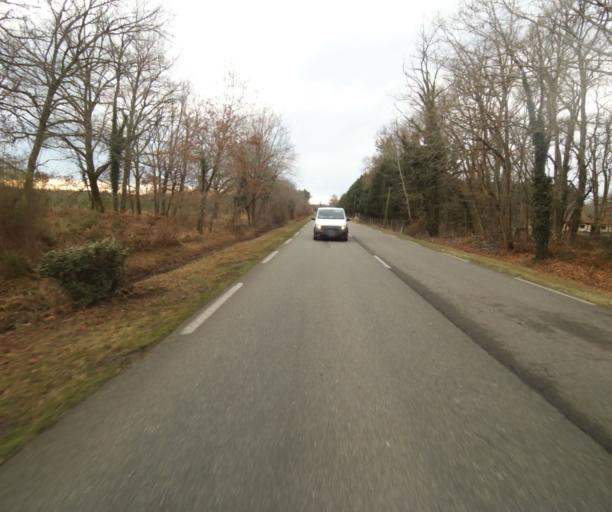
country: FR
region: Aquitaine
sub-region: Departement des Landes
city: Gabarret
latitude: 44.0973
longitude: -0.0178
